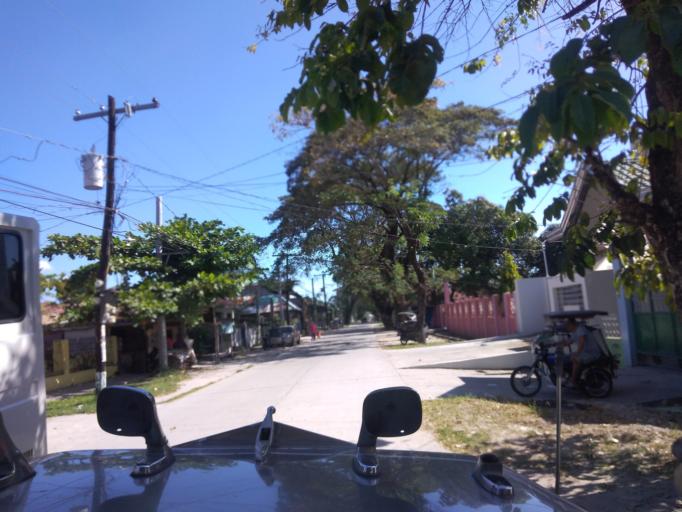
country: PH
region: Central Luzon
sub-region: Province of Pampanga
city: San Agustin
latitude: 14.9893
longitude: 120.5966
